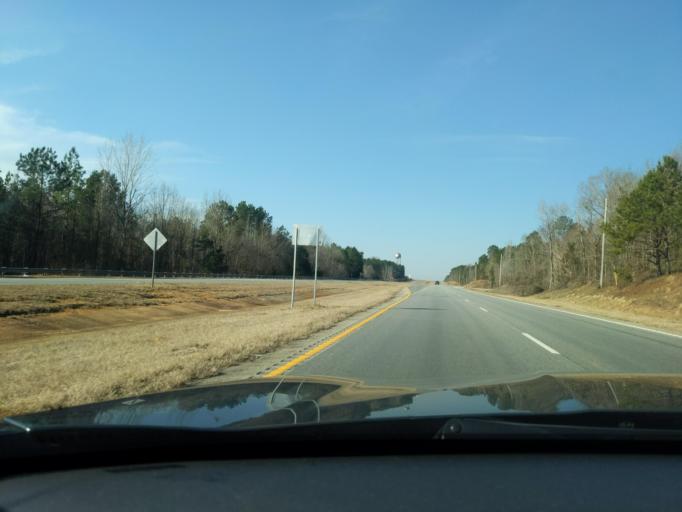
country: US
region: South Carolina
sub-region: Abbeville County
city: Calhoun Falls
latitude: 34.1102
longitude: -82.5144
